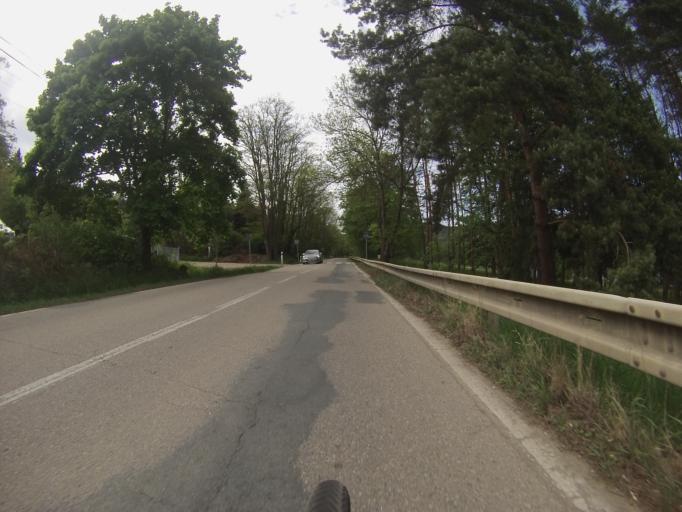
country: CZ
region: South Moravian
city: Kurim
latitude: 49.2429
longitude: 16.4986
